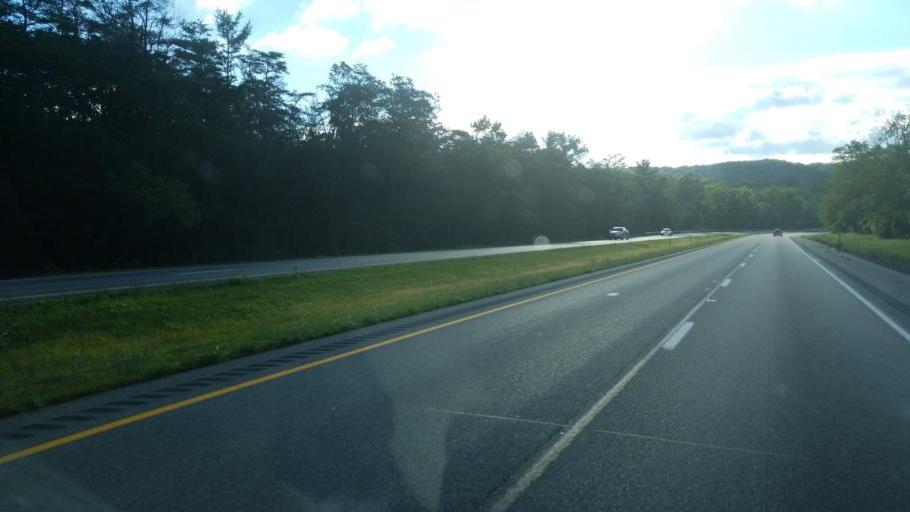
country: US
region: Maryland
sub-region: Washington County
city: Hancock
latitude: 39.7945
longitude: -78.2195
